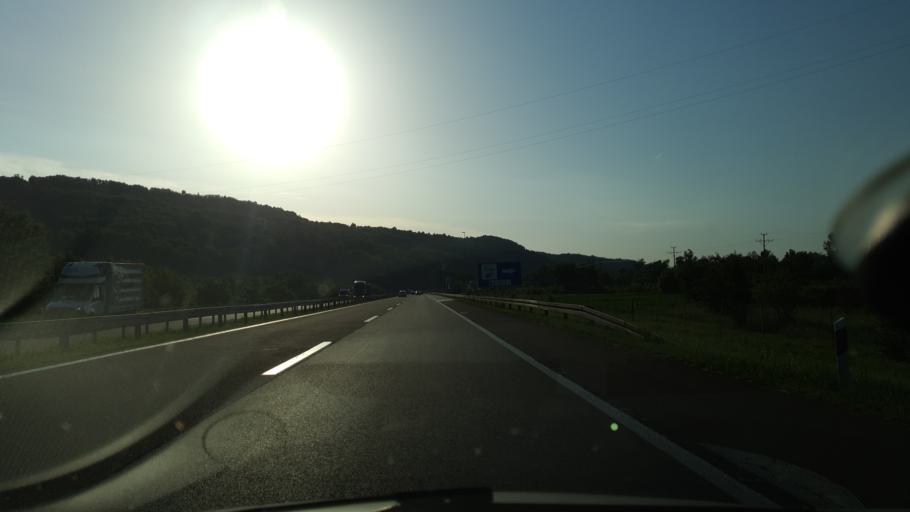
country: RS
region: Central Serbia
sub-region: Pomoravski Okrug
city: Jagodina
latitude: 44.0613
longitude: 21.2106
